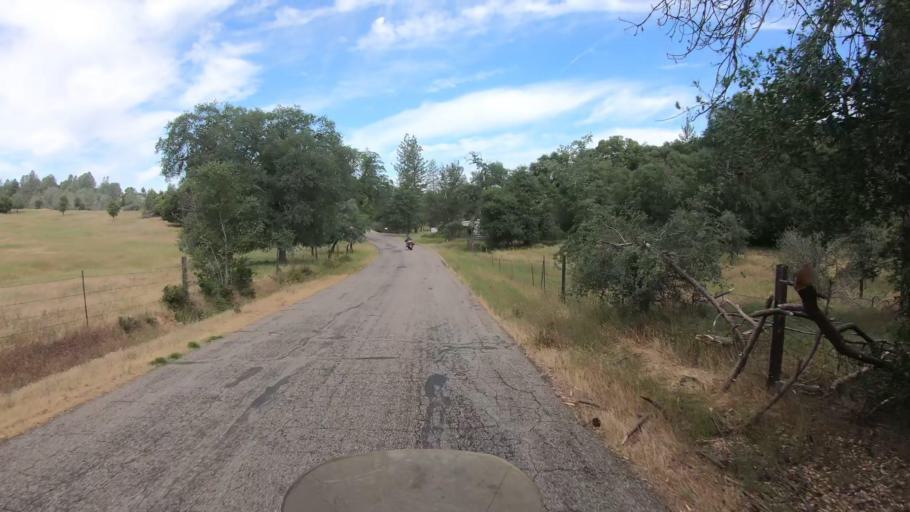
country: US
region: California
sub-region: Tuolumne County
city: Tuolumne City
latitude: 37.8448
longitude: -120.1342
